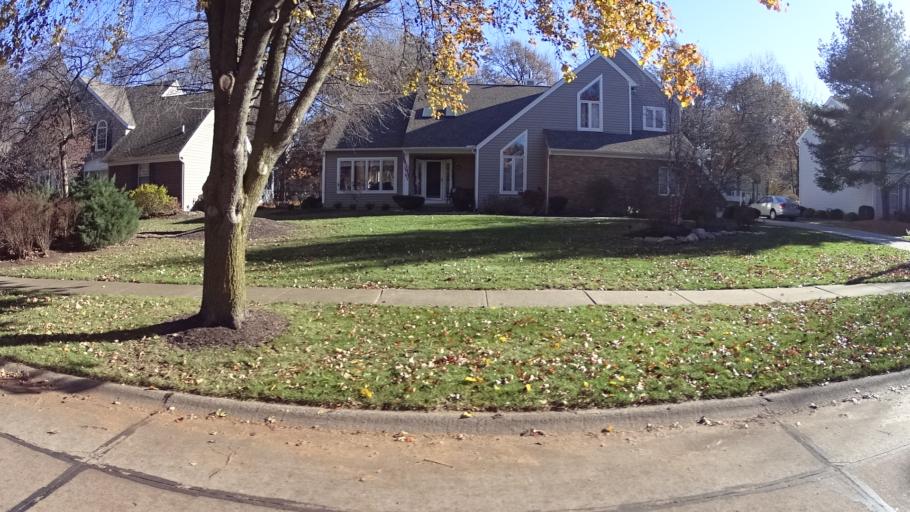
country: US
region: Ohio
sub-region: Lorain County
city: Avon Lake
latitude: 41.4993
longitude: -81.9822
